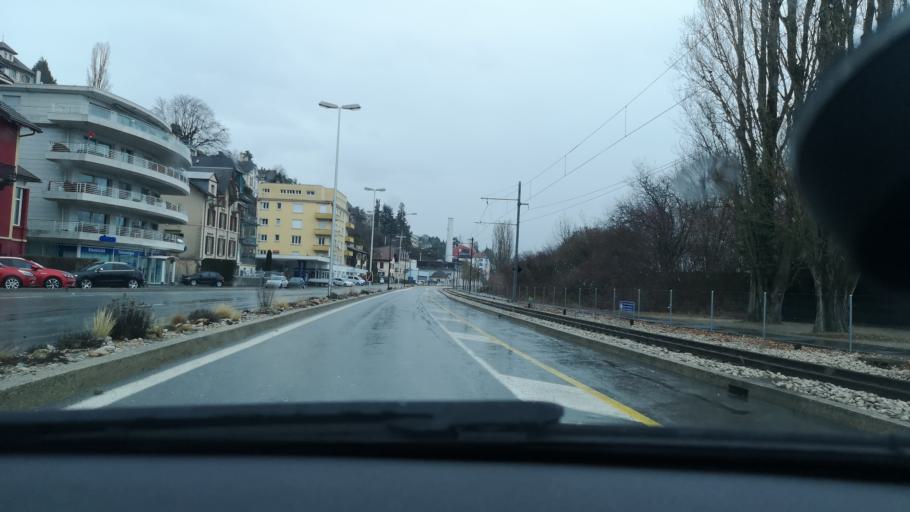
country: CH
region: Neuchatel
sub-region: Neuchatel District
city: Neuchatel
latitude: 46.9848
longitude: 6.9123
